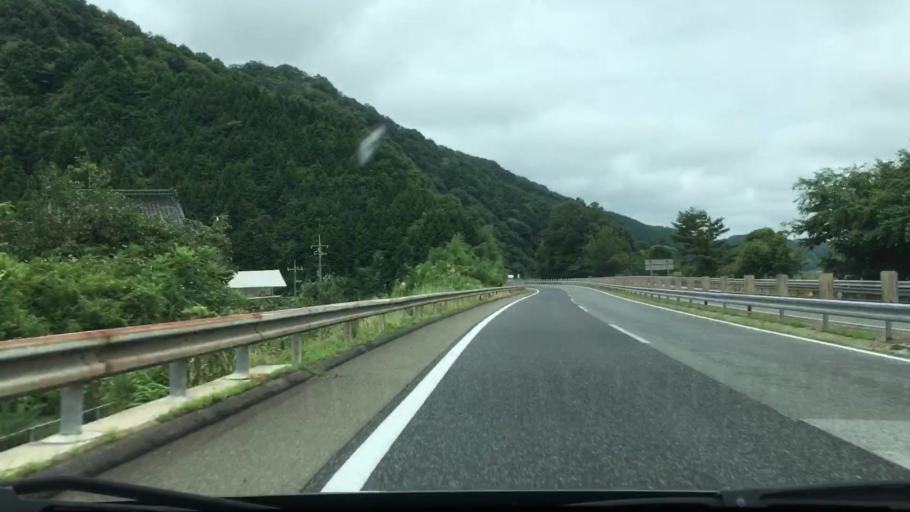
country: JP
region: Hiroshima
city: Shobara
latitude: 34.8365
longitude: 133.0815
